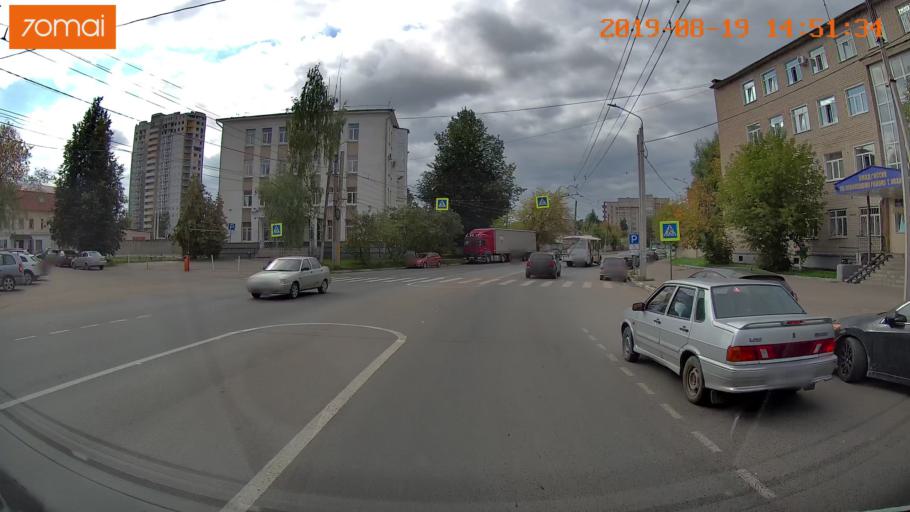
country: RU
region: Ivanovo
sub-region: Gorod Ivanovo
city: Ivanovo
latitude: 56.9947
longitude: 40.9973
